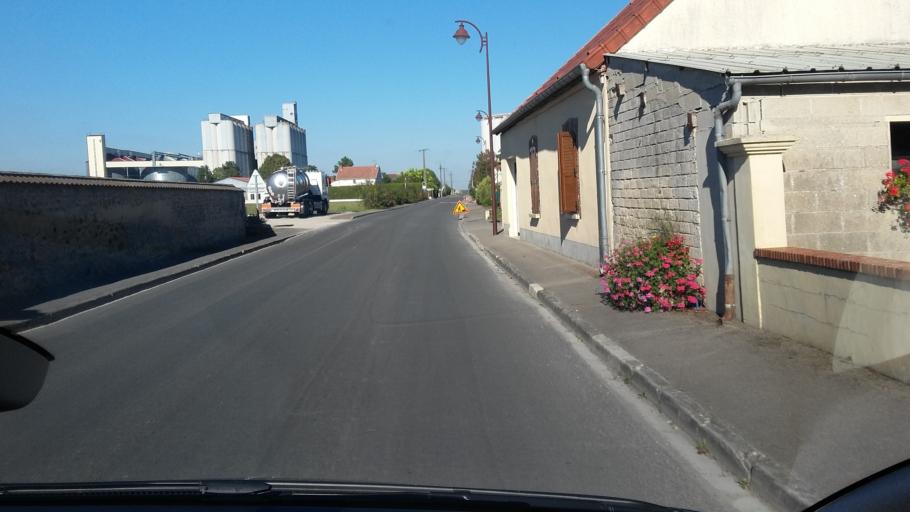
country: FR
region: Champagne-Ardenne
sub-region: Departement de la Marne
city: Vertus
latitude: 48.8479
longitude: 3.9666
